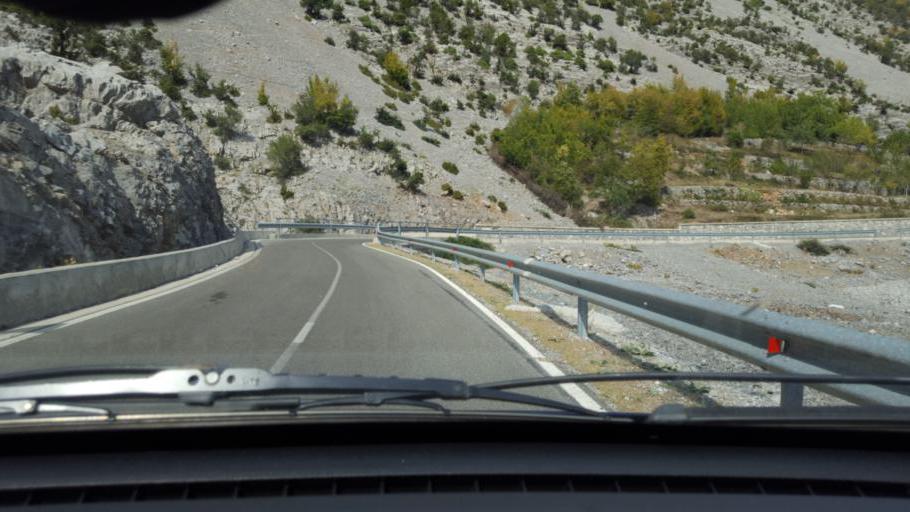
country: AL
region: Shkoder
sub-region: Rrethi i Malesia e Madhe
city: Kastrat
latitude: 42.4986
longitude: 19.5818
